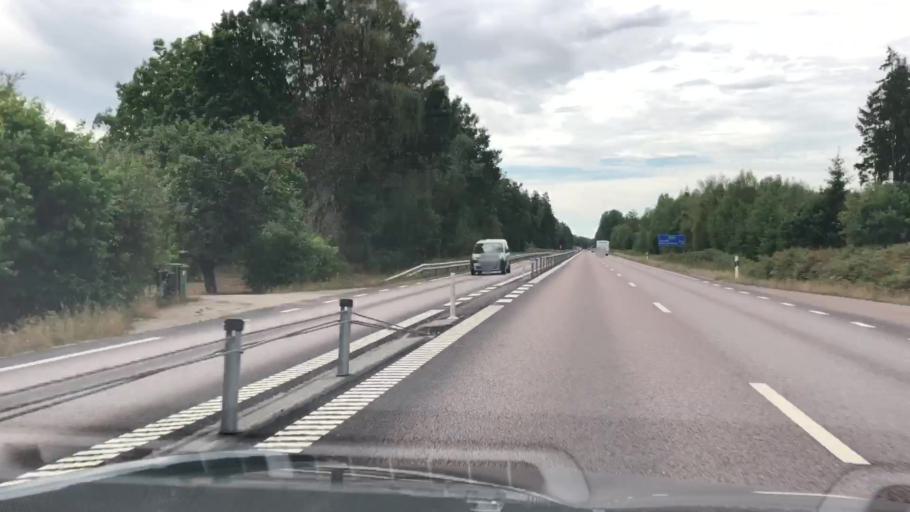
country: SE
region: Blekinge
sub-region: Karlskrona Kommun
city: Jaemjoe
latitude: 56.2517
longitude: 15.9407
